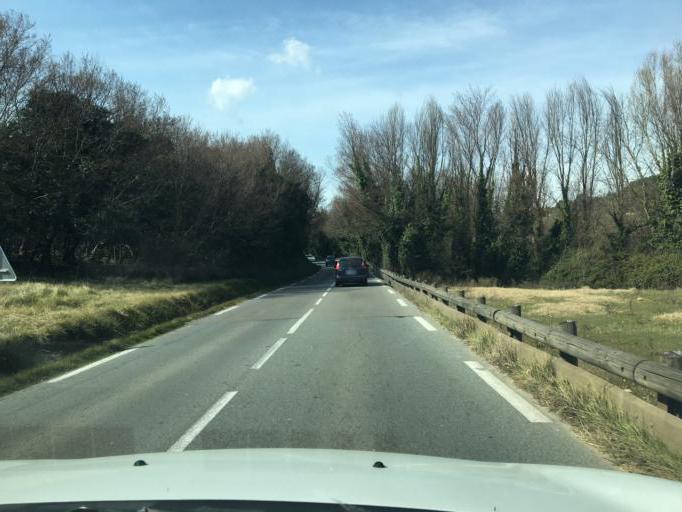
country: FR
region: Provence-Alpes-Cote d'Azur
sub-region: Departement du Var
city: Flayosc
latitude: 43.5348
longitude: 6.4035
